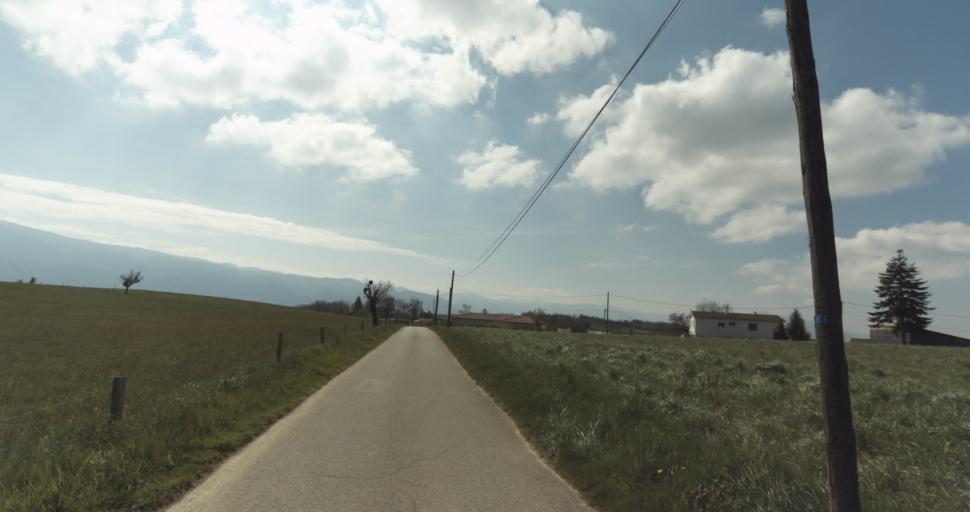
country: FR
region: Rhone-Alpes
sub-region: Departement de l'Isere
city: Saint-Verand
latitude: 45.1726
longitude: 5.3066
